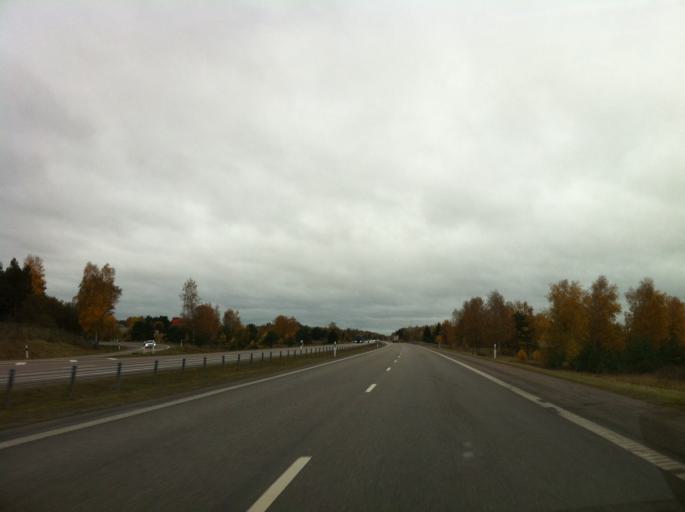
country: SE
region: OEstergoetland
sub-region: Mjolby Kommun
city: Mantorp
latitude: 58.3719
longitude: 15.3015
